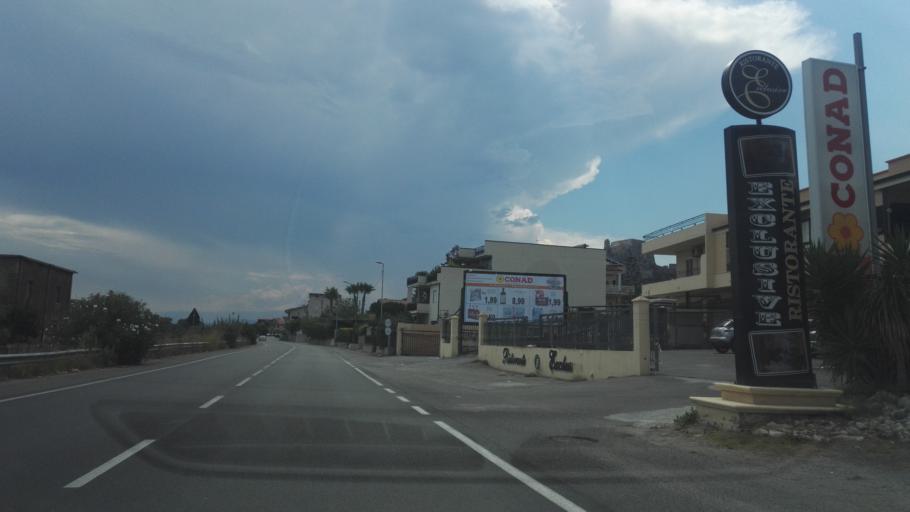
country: IT
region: Calabria
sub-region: Provincia di Reggio Calabria
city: Roccella Ionica
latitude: 38.3255
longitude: 16.4168
